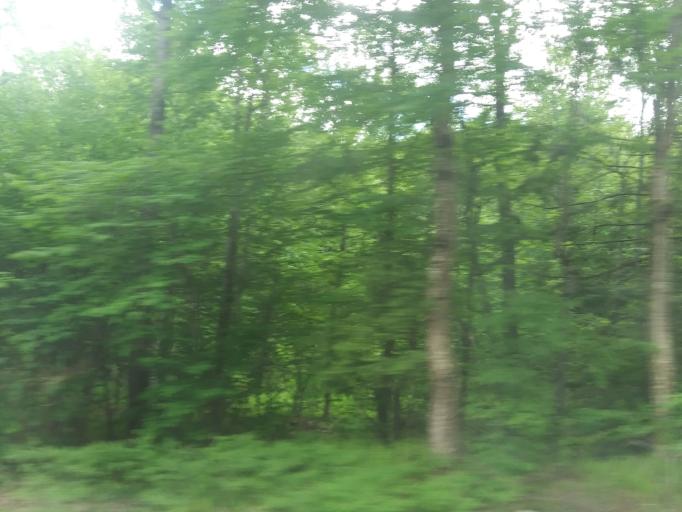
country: US
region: Massachusetts
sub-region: Franklin County
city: Shelburne Falls
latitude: 42.5844
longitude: -72.7462
